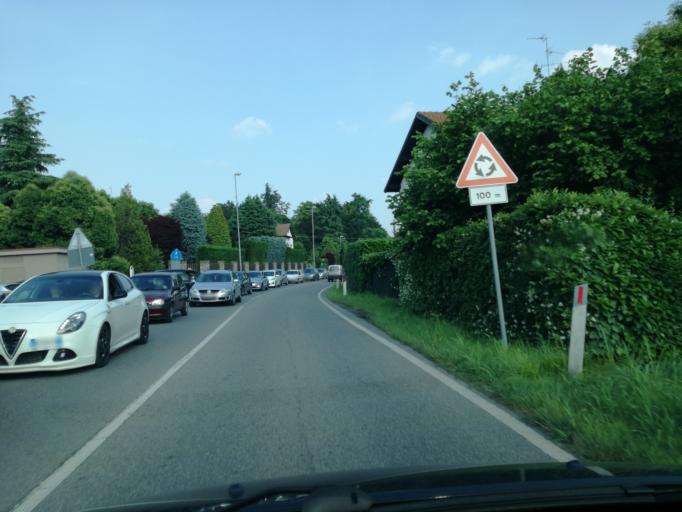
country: IT
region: Lombardy
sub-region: Provincia di Lecco
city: Robbiate
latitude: 45.6853
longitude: 9.4395
